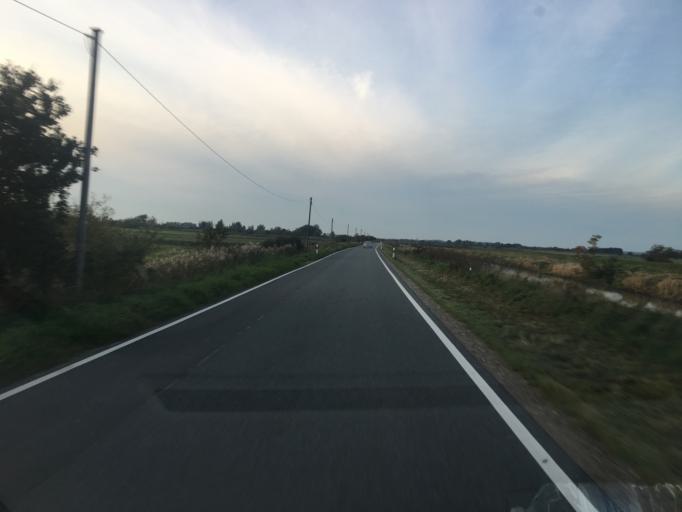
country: DE
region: Schleswig-Holstein
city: Aventoft
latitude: 54.9017
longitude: 8.8411
